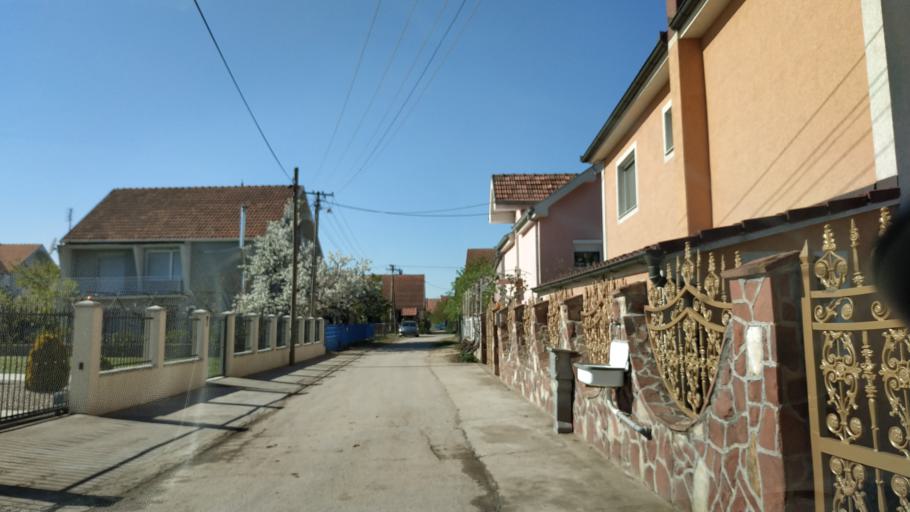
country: RS
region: Central Serbia
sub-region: Nisavski Okrug
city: Aleksinac
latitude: 43.4978
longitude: 21.6945
